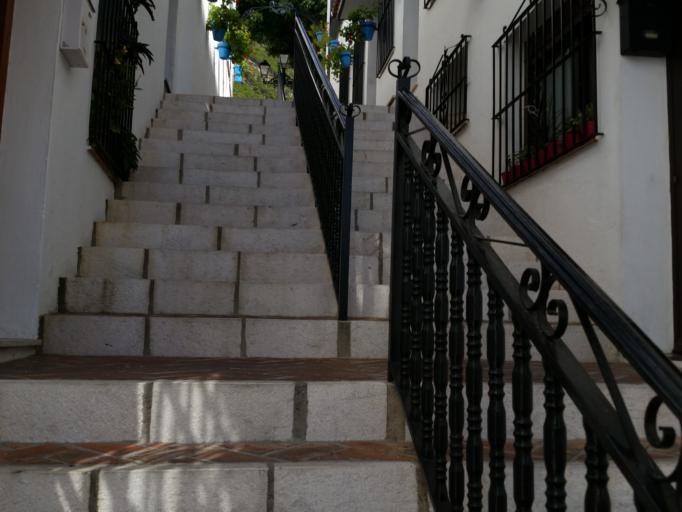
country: ES
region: Andalusia
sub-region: Provincia de Malaga
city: Mijas
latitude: 36.5971
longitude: -4.6370
